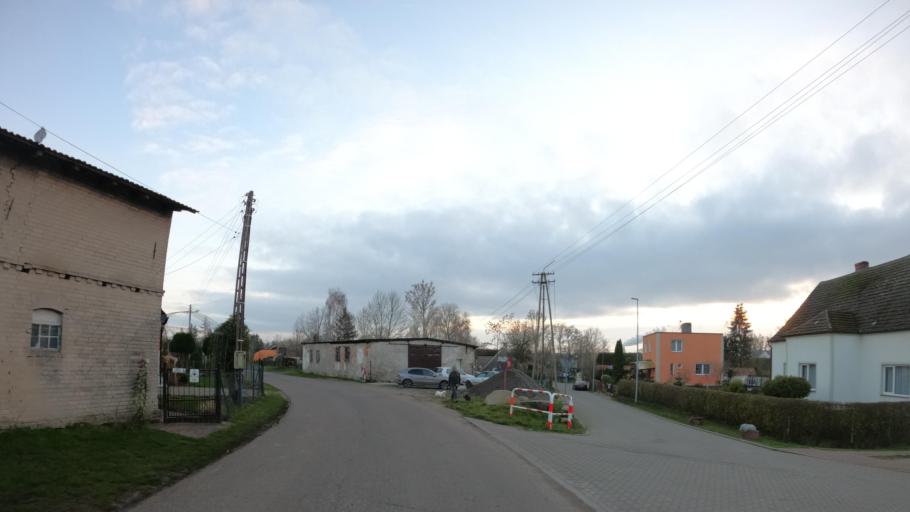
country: PL
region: West Pomeranian Voivodeship
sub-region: Powiat bialogardzki
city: Karlino
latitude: 54.0792
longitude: 15.8812
